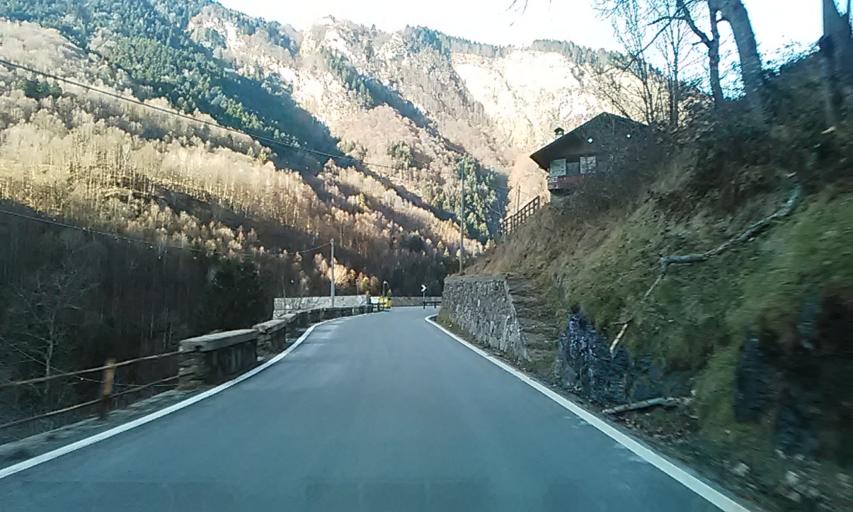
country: IT
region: Piedmont
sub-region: Provincia di Vercelli
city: Boccioleto
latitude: 45.8312
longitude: 8.0929
